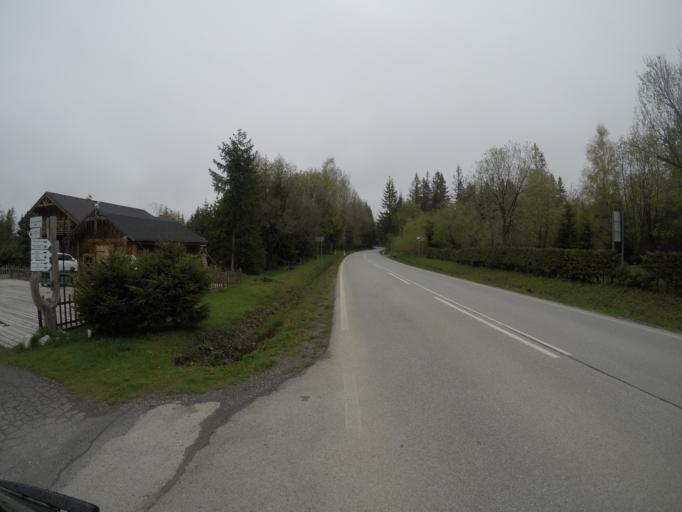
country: SK
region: Presovsky
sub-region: Okres Poprad
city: Strba
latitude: 49.0934
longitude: 20.0691
